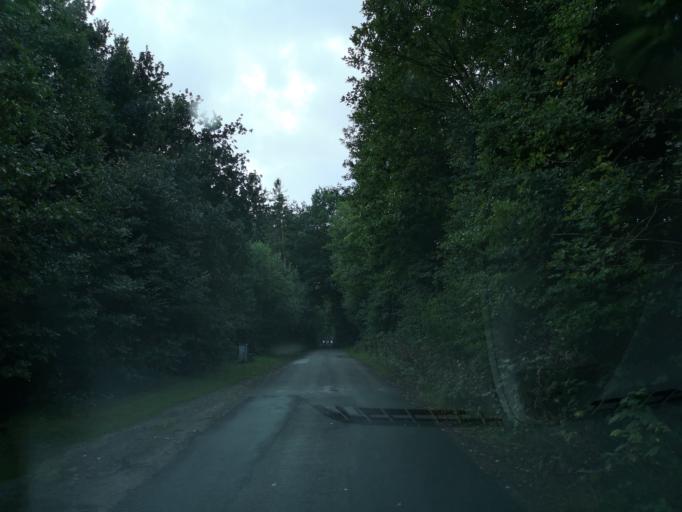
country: DK
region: Central Jutland
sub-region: Holstebro Kommune
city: Holstebro
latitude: 56.3363
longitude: 8.6386
